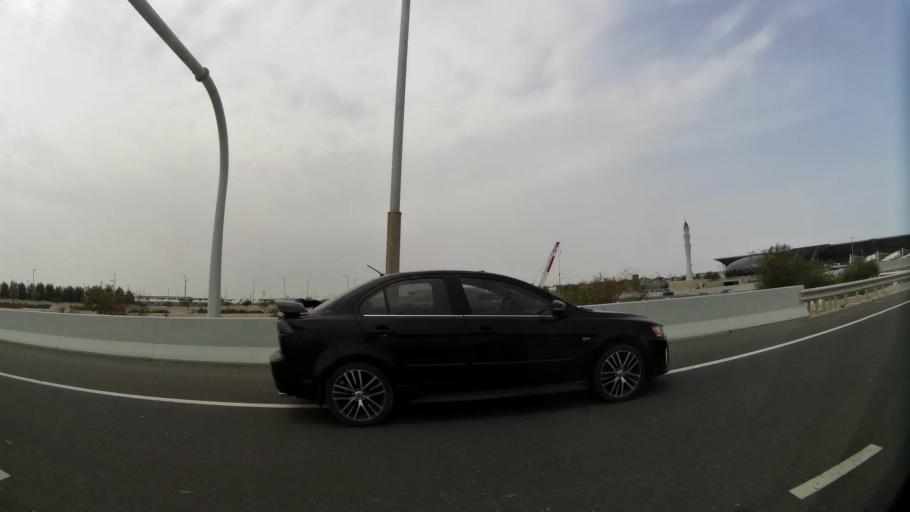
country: QA
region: Al Wakrah
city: Al Wakrah
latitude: 25.2564
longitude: 51.6167
